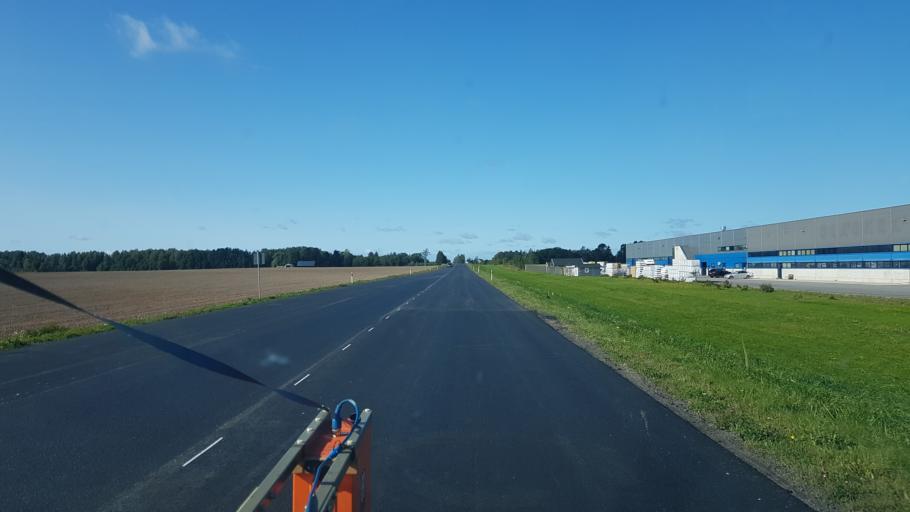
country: EE
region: Tartu
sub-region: Noo vald
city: Noo
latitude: 58.3542
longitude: 26.5943
